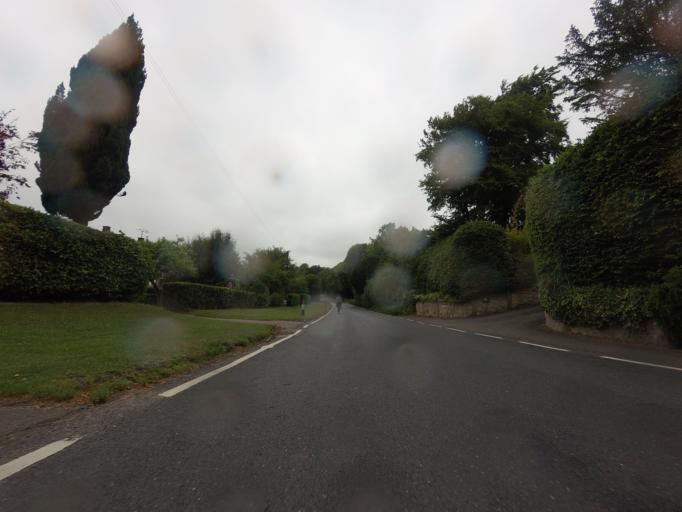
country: GB
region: England
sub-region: Kent
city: Kemsing
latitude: 51.3104
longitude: 0.2154
